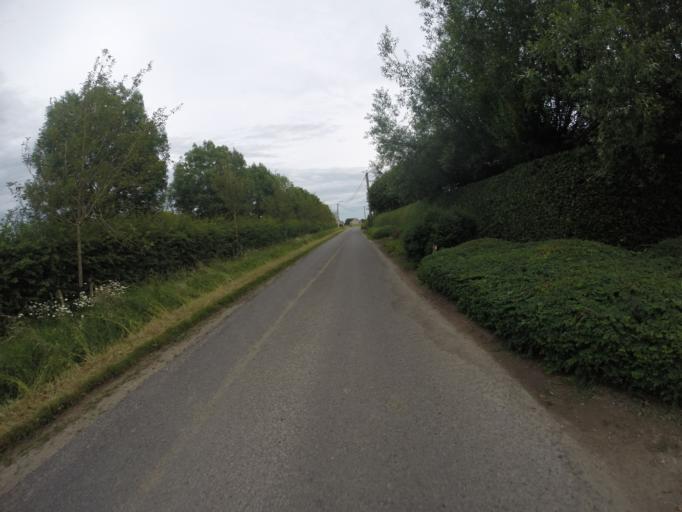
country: BE
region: Flanders
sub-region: Provincie West-Vlaanderen
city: Ruiselede
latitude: 51.0182
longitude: 3.3813
